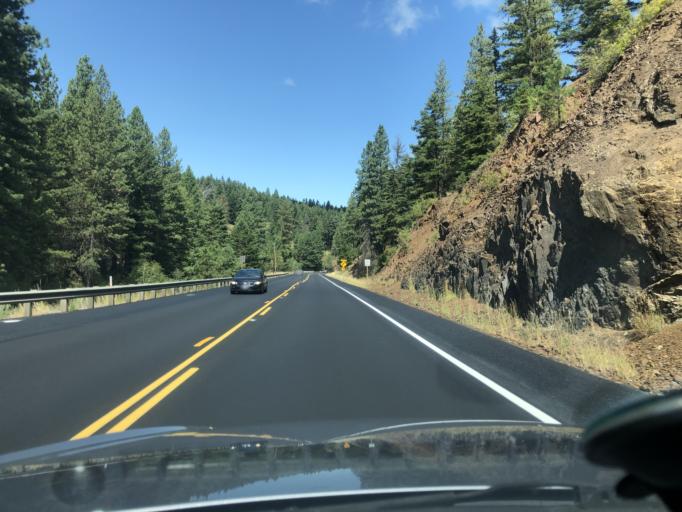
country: US
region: Washington
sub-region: Kittitas County
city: Cle Elum
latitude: 47.2397
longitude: -120.6957
